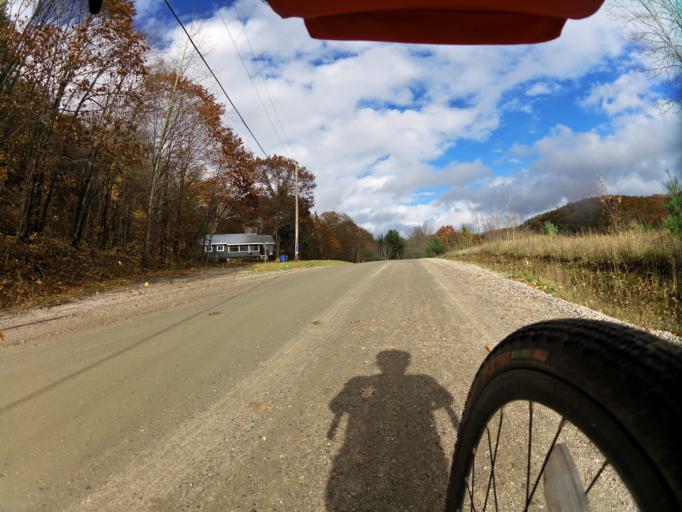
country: CA
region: Quebec
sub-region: Outaouais
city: Wakefield
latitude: 45.7033
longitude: -76.0238
